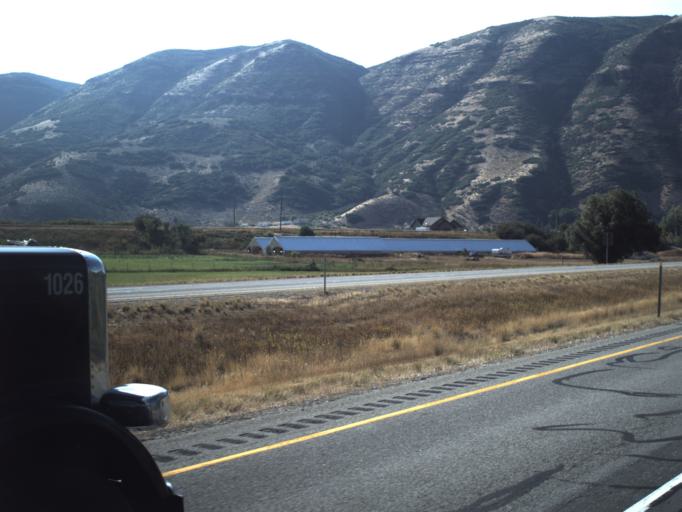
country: US
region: Utah
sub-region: Morgan County
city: Morgan
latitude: 41.0389
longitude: -111.5142
